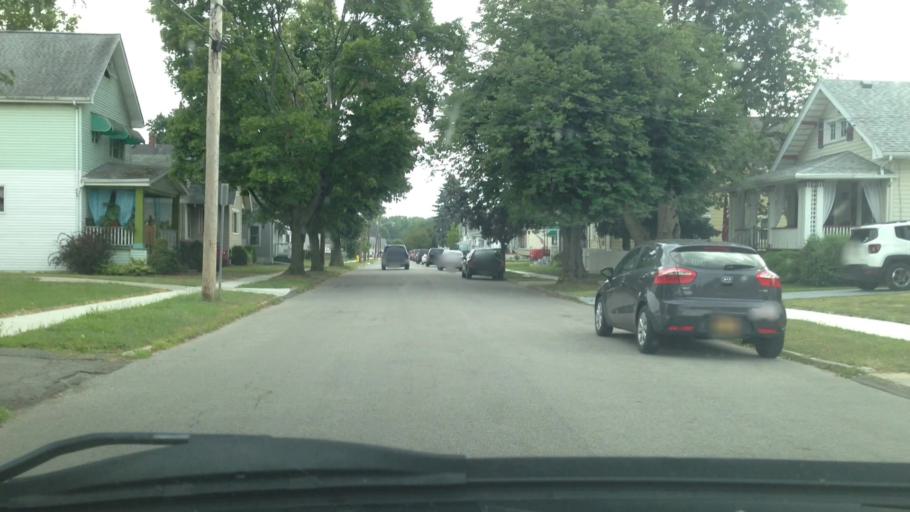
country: US
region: New York
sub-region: Erie County
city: Sloan
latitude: 42.8741
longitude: -78.7969
